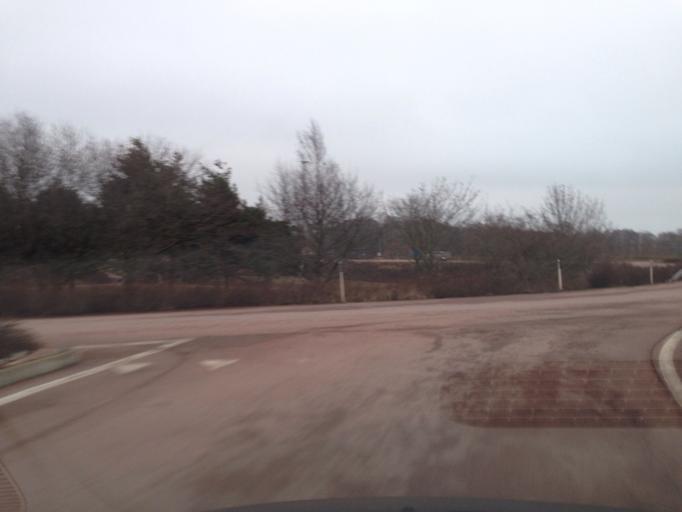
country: AX
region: Mariehamns stad
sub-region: Mariehamn
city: Mariehamn
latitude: 60.1143
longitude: 19.9389
